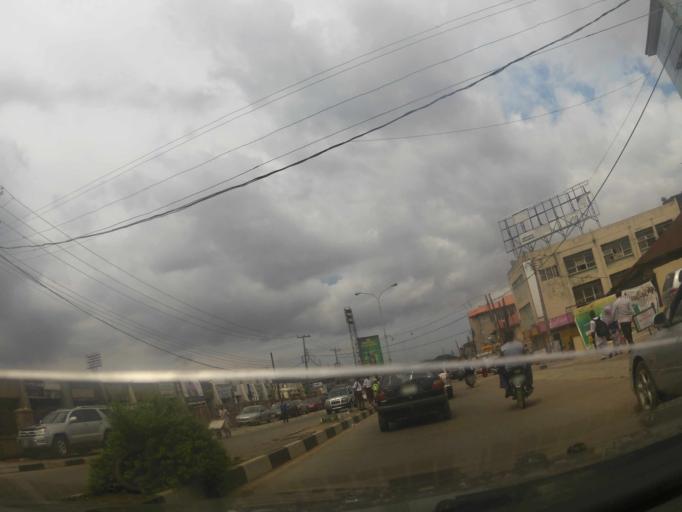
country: NG
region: Oyo
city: Ibadan
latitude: 7.3941
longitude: 3.8846
